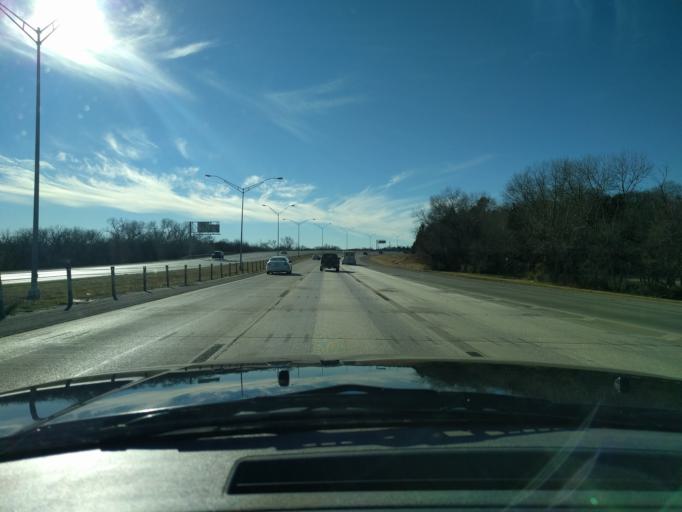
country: US
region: Oklahoma
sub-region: Oklahoma County
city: Nichols Hills
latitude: 35.5348
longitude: -97.4802
